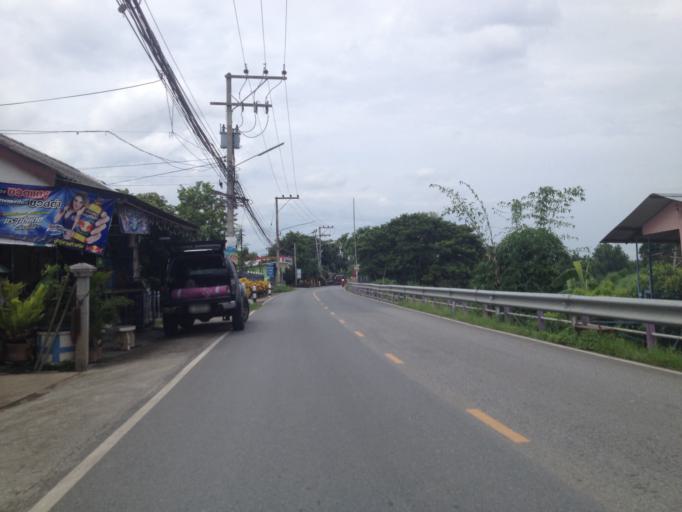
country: TH
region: Chiang Mai
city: Saraphi
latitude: 18.7083
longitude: 98.9826
